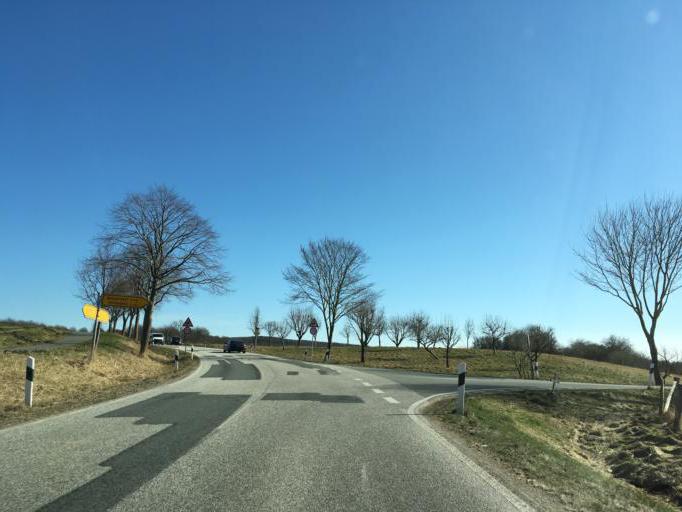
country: DE
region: Schleswig-Holstein
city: Berkenthin
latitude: 53.7299
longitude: 10.6531
